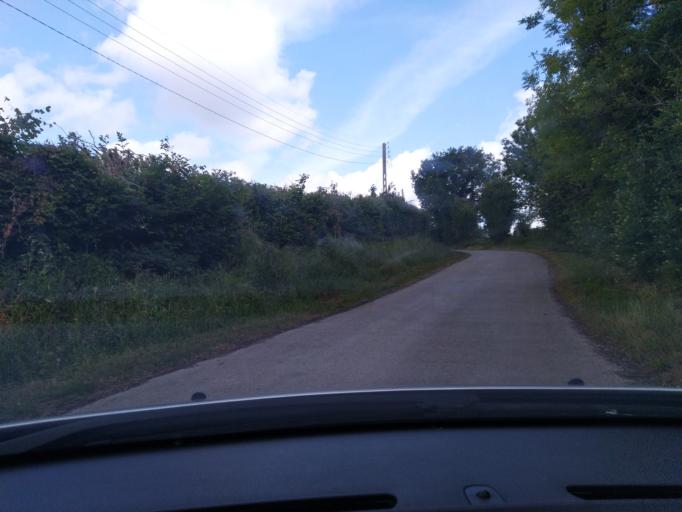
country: FR
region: Nord-Pas-de-Calais
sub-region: Departement du Pas-de-Calais
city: Ferques
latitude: 50.8356
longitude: 1.7568
